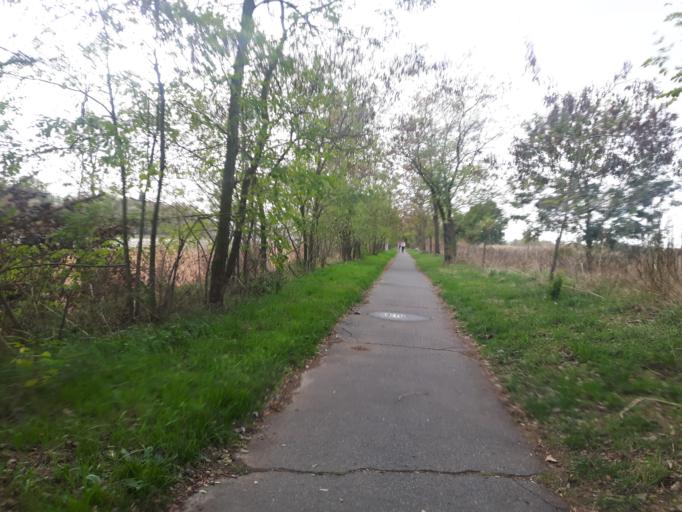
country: DE
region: Rheinland-Pfalz
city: Urmitz
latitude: 50.4199
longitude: 7.5134
